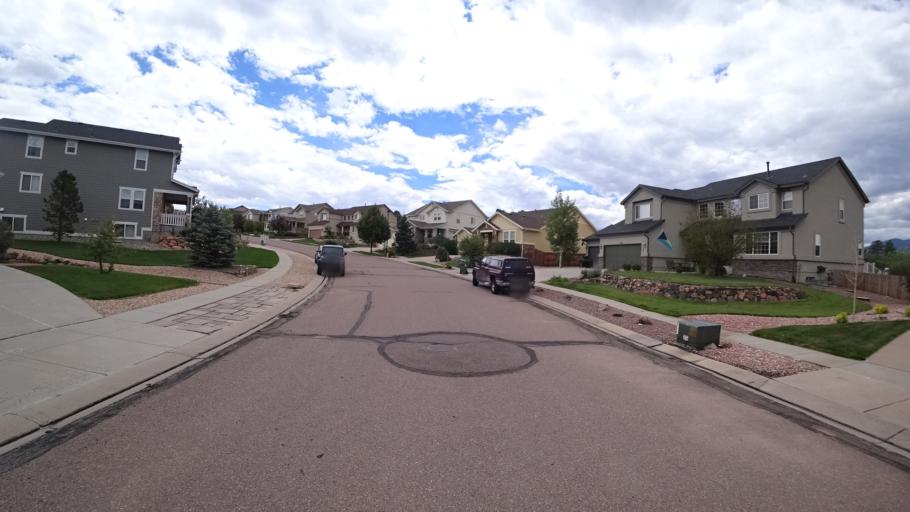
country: US
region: Colorado
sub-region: El Paso County
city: Gleneagle
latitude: 39.0333
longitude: -104.8165
